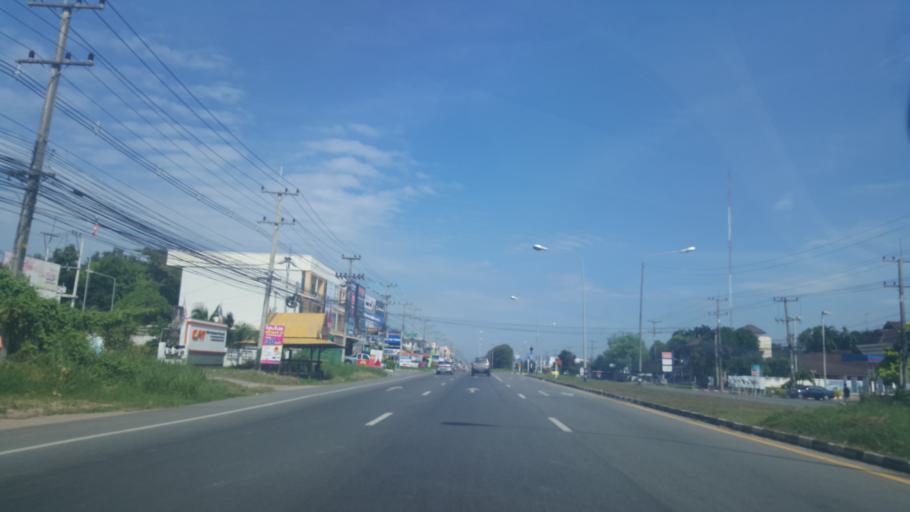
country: TH
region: Chon Buri
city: Sattahip
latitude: 12.6905
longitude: 100.8921
